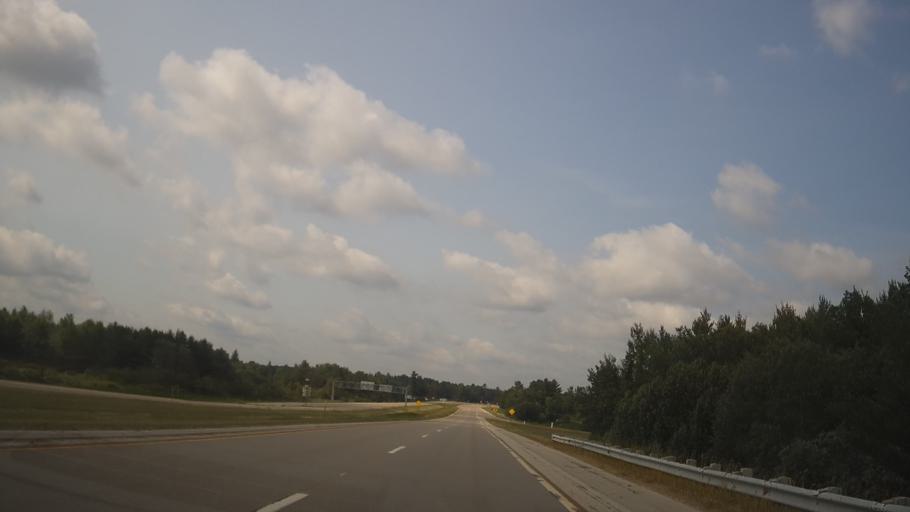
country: US
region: Michigan
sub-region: Roscommon County
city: Saint Helen
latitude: 44.3126
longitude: -84.5066
